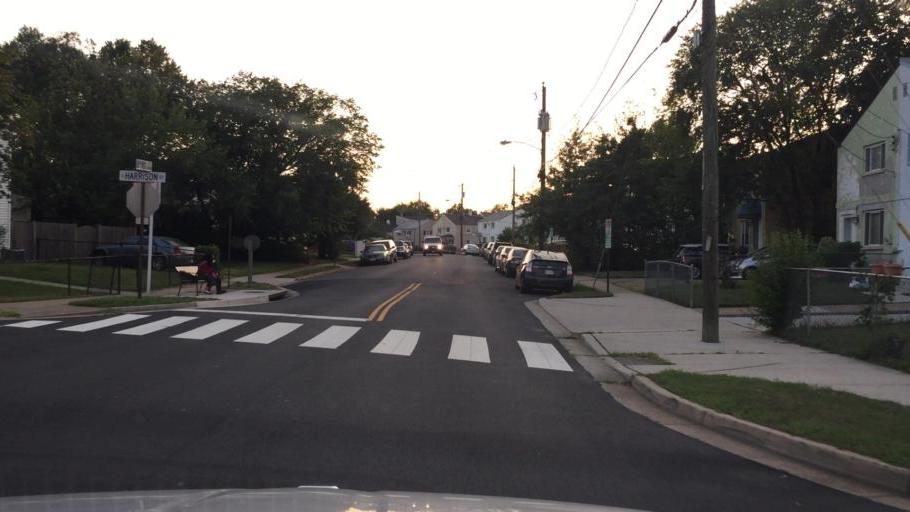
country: US
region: Virginia
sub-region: Fairfax County
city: Baileys Crossroads
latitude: 38.8563
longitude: -77.1211
